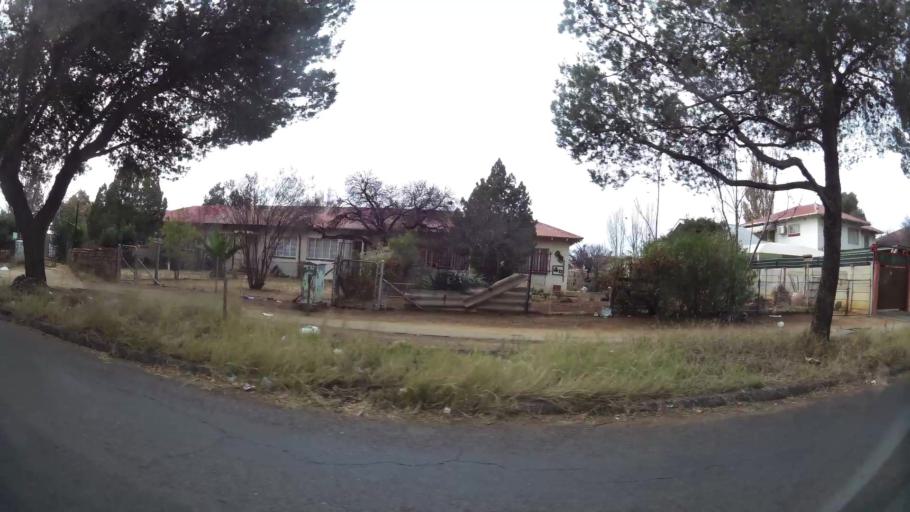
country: ZA
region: Orange Free State
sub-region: Mangaung Metropolitan Municipality
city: Bloemfontein
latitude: -29.1274
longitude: 26.1909
